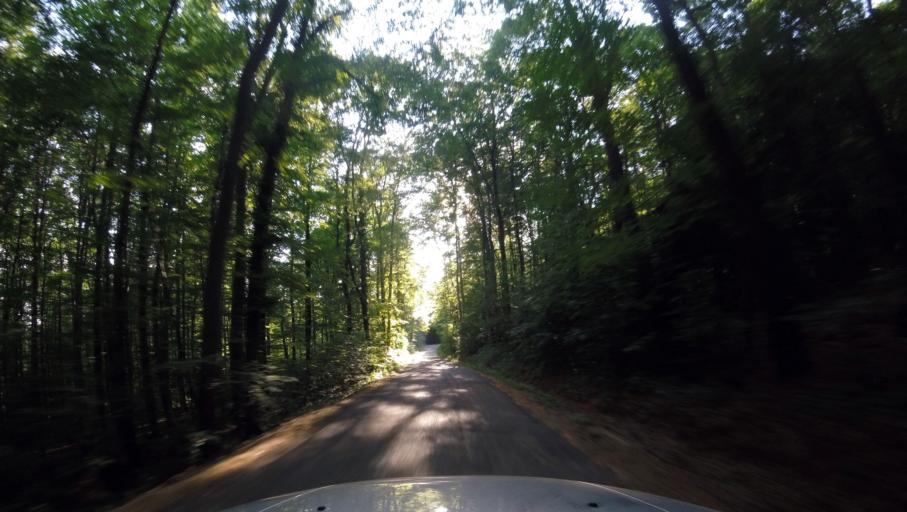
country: DE
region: Baden-Wuerttemberg
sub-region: Regierungsbezirk Stuttgart
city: Spiegelberg
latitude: 49.0363
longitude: 9.4240
